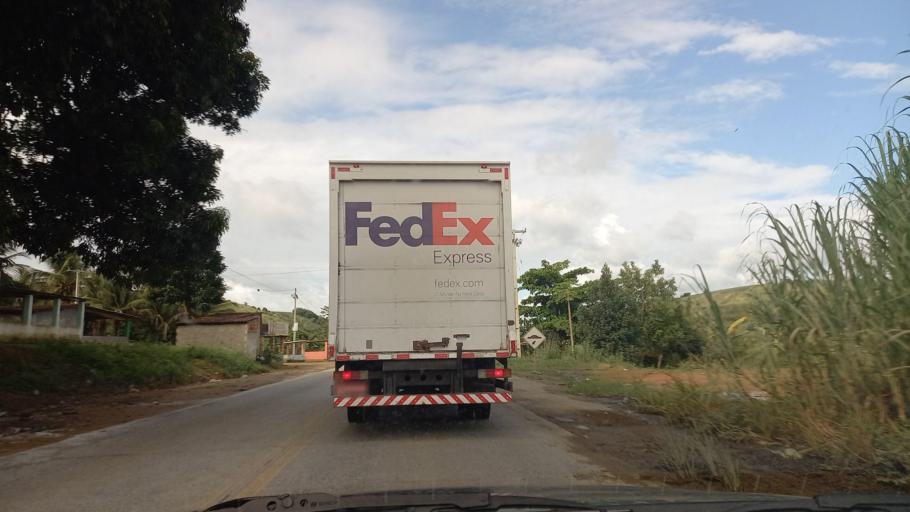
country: BR
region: Pernambuco
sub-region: Palmares
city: Palmares
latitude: -8.6922
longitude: -35.6384
